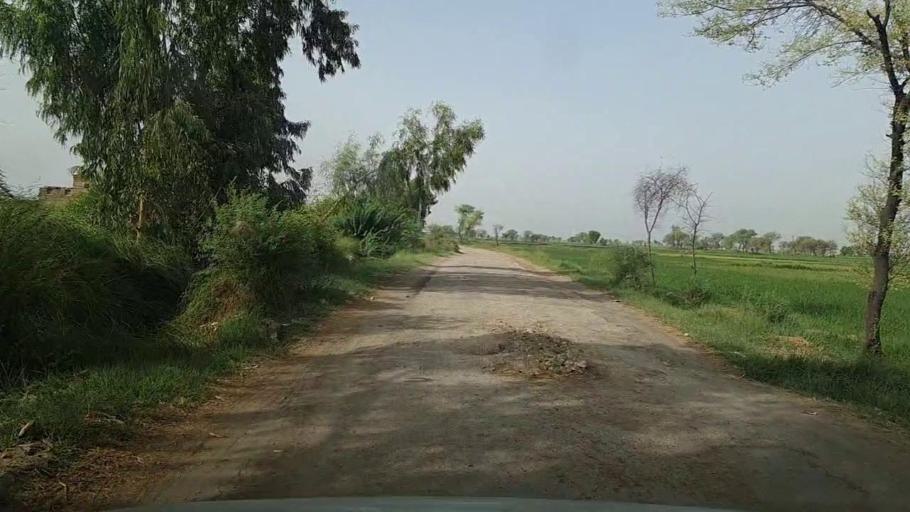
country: PK
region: Sindh
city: Mehar
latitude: 27.1177
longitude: 67.8206
